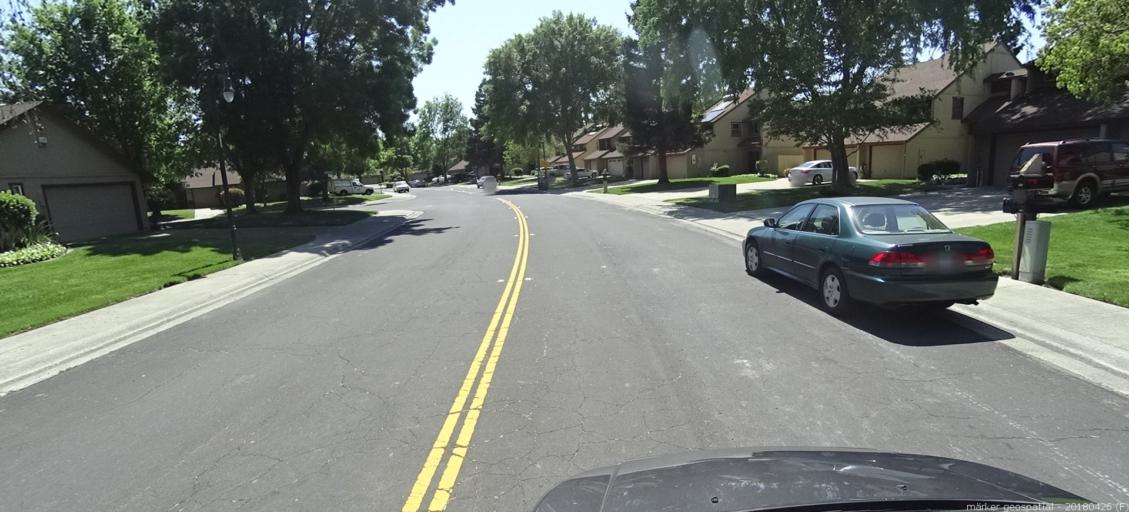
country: US
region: California
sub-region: Yolo County
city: West Sacramento
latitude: 38.5488
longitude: -121.5486
